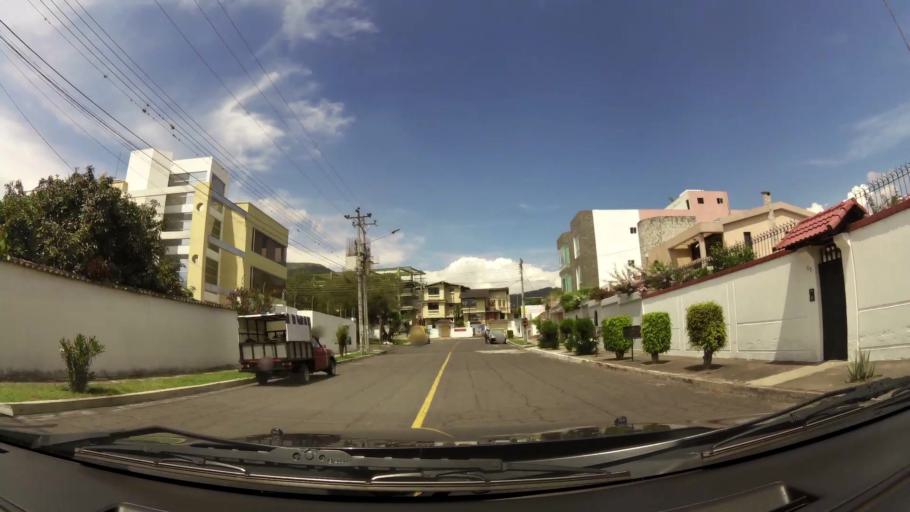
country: EC
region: Pichincha
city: Quito
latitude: -0.2163
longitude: -78.4252
